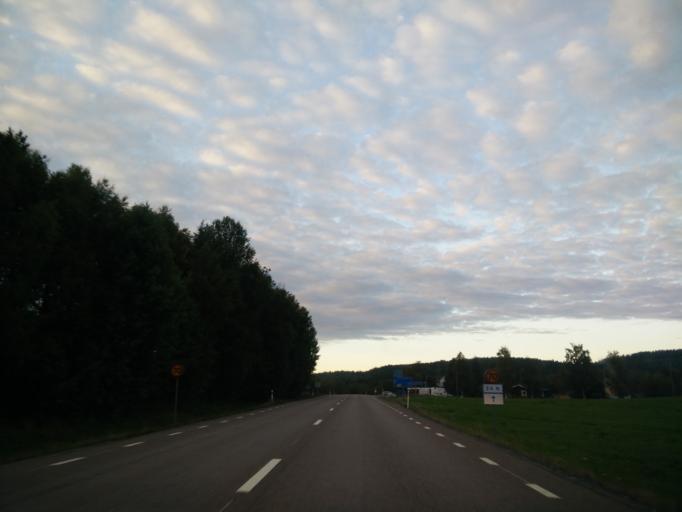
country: SE
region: Vaesternorrland
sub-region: Kramfors Kommun
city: Nordingra
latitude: 62.9285
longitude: 18.0839
